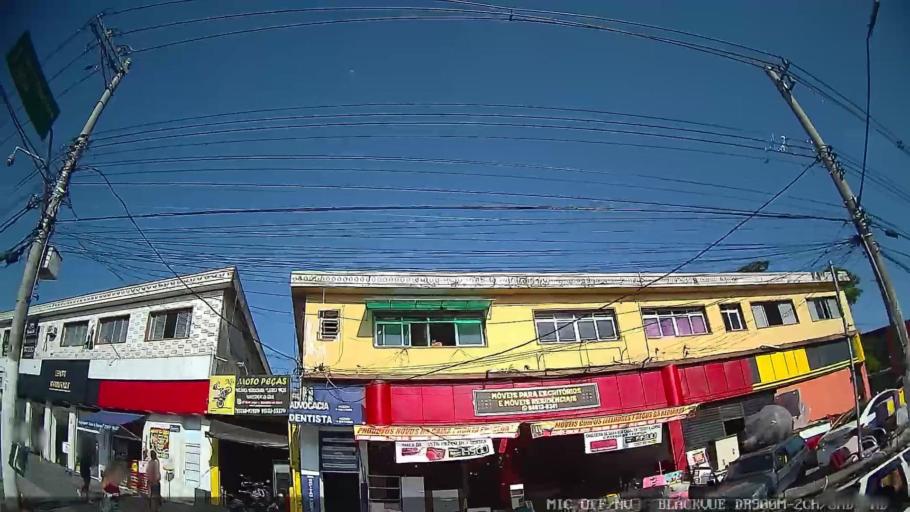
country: BR
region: Sao Paulo
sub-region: Ferraz De Vasconcelos
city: Ferraz de Vasconcelos
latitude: -23.5395
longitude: -46.4082
